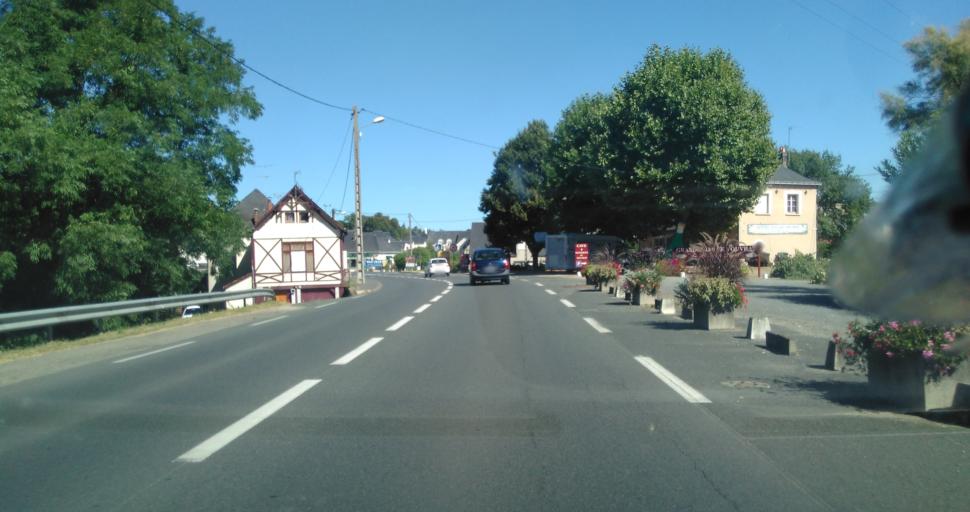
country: FR
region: Centre
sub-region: Departement d'Indre-et-Loire
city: Vouvray
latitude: 47.4082
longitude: 0.7992
